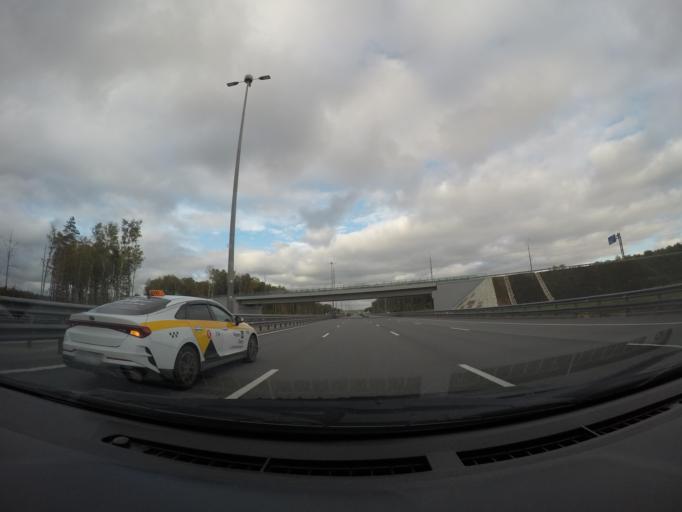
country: RU
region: Moskovskaya
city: Barvikha
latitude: 55.7108
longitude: 37.3136
